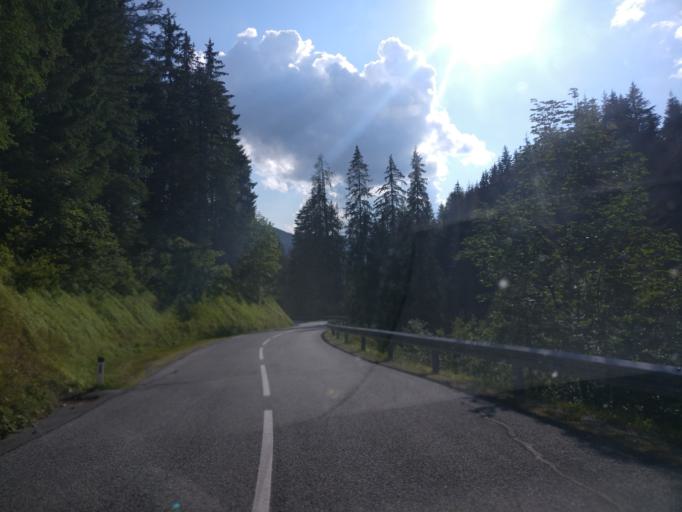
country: AT
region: Salzburg
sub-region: Politischer Bezirk Sankt Johann im Pongau
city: Muhlbach am Hochkonig
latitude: 47.4015
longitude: 13.1158
